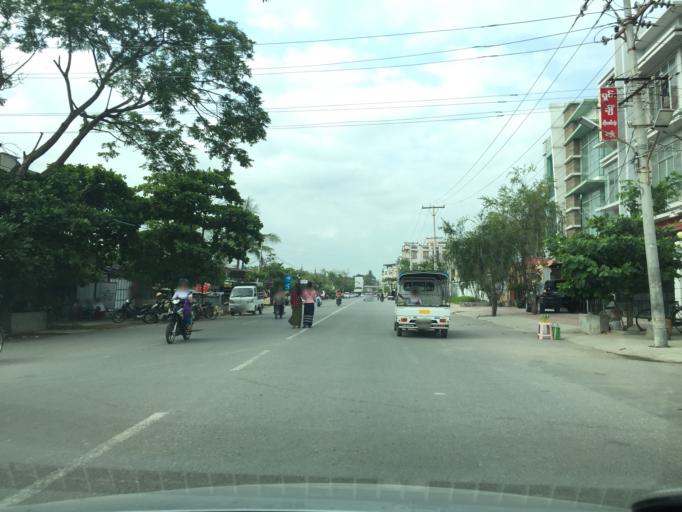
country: MM
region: Mandalay
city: Mandalay
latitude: 21.9714
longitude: 96.1030
